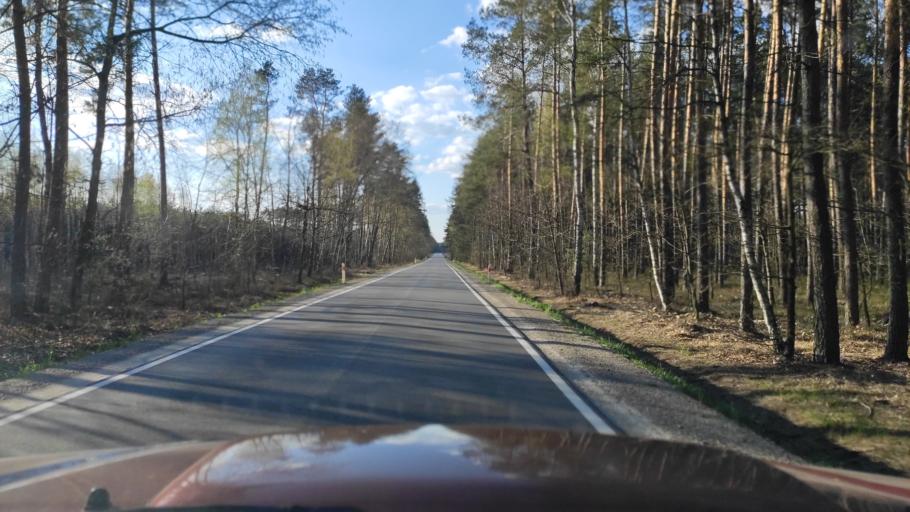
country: PL
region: Masovian Voivodeship
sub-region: Powiat zwolenski
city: Zwolen
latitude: 51.3920
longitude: 21.5476
